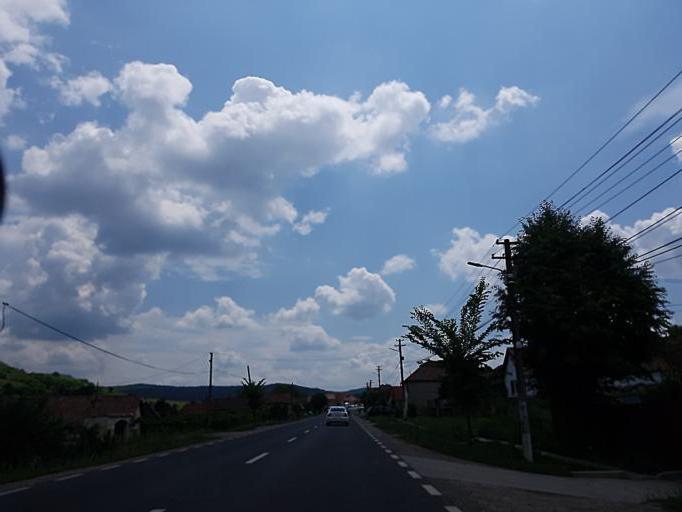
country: RO
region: Sibiu
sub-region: Comuna Slimnic
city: Slimnic
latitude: 45.9085
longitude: 24.1575
